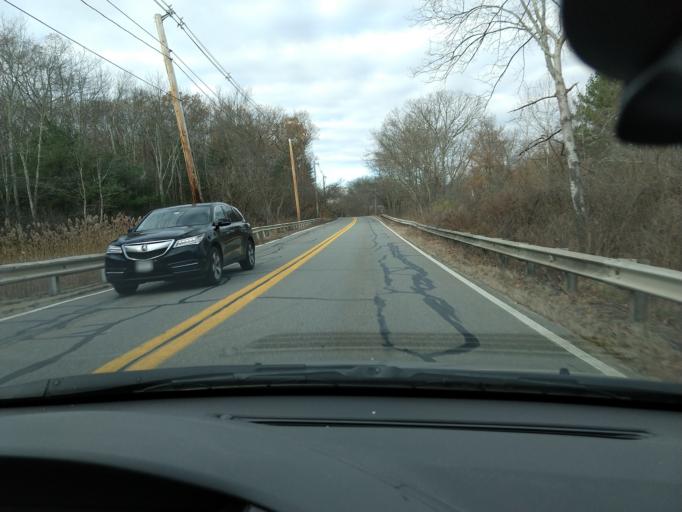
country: US
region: Massachusetts
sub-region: Middlesex County
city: Lincoln
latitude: 42.4485
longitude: -71.2716
